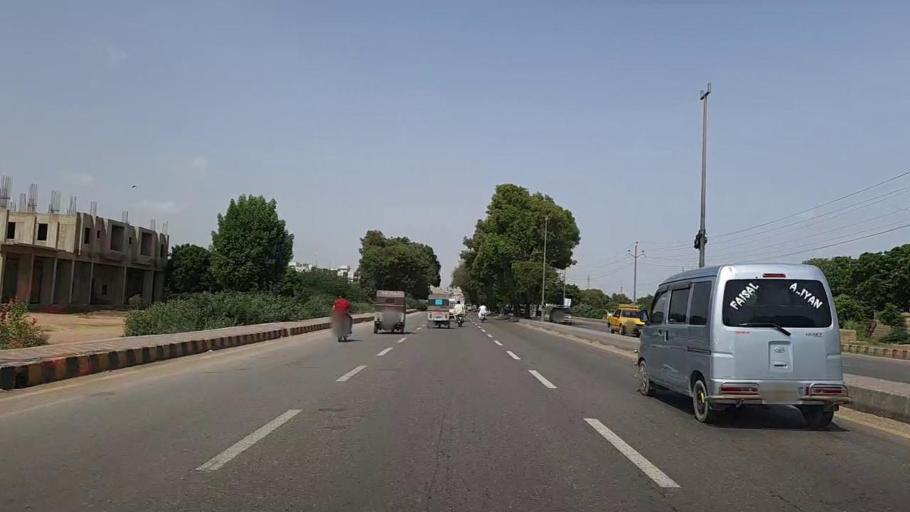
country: PK
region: Sindh
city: Malir Cantonment
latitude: 24.8536
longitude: 67.2500
